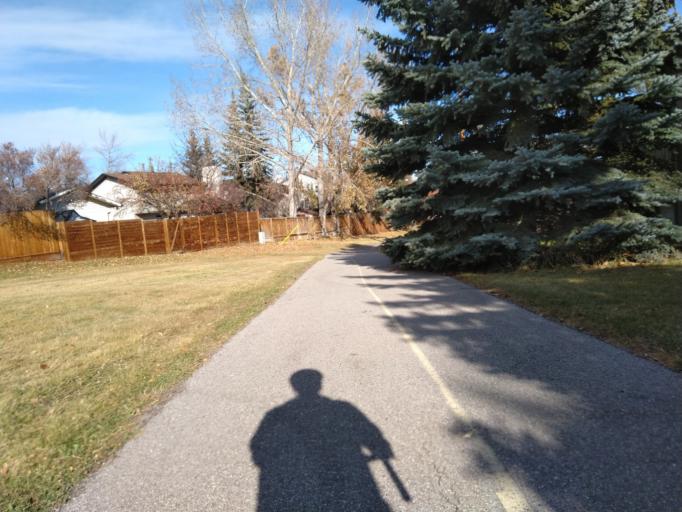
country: CA
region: Alberta
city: Calgary
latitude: 51.1255
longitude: -114.0861
